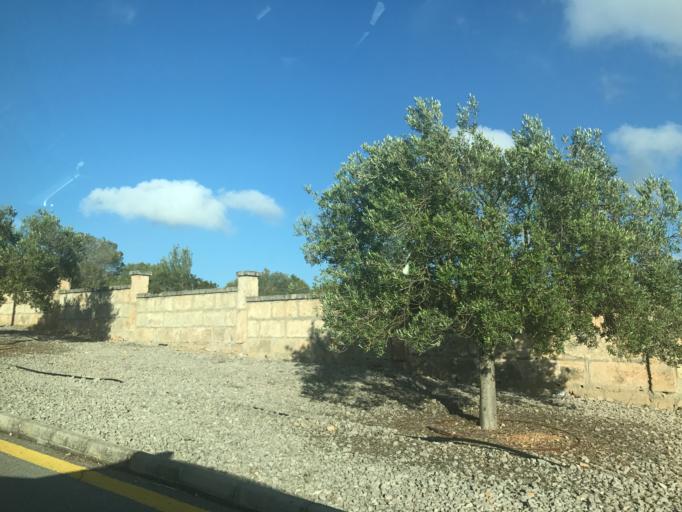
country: ES
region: Balearic Islands
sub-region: Illes Balears
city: s'Arenal
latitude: 39.5342
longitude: 2.7940
